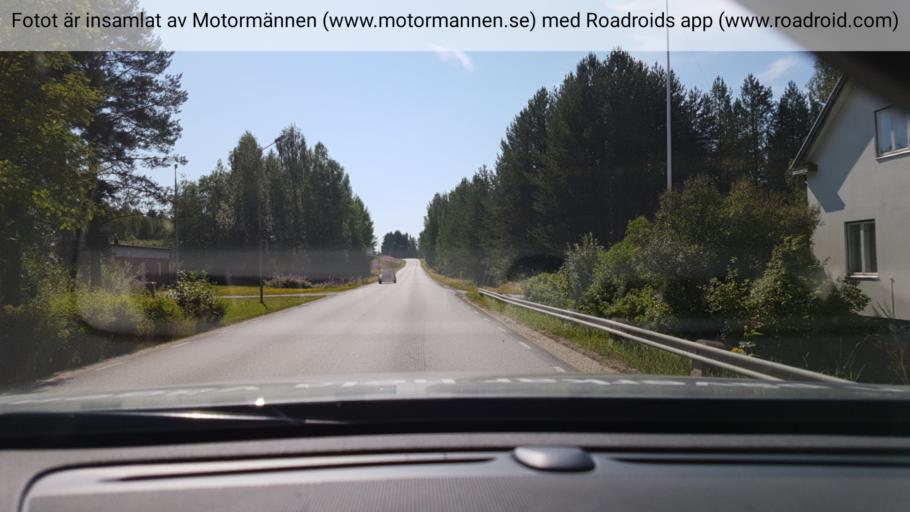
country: SE
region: Vaesterbotten
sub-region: Vindelns Kommun
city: Vindeln
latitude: 64.2250
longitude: 19.7069
